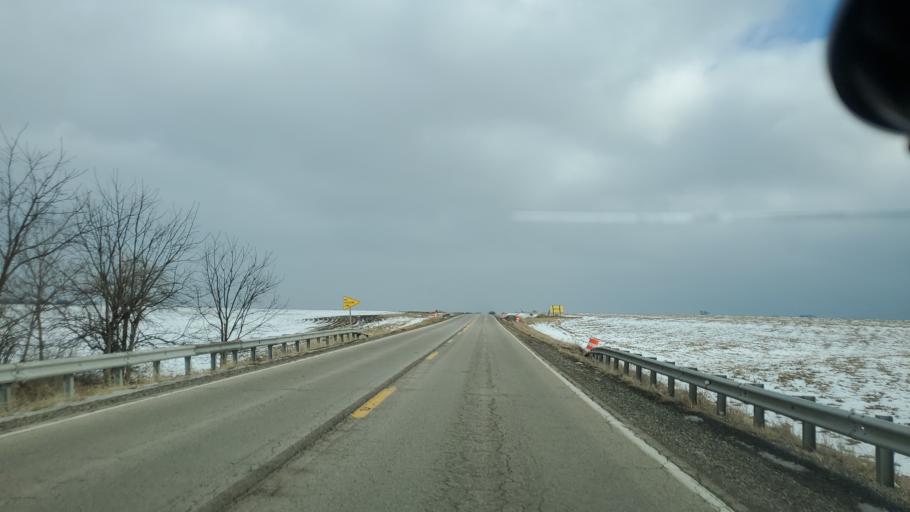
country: US
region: Illinois
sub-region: Marshall County
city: Toluca
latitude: 41.1186
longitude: -89.1871
